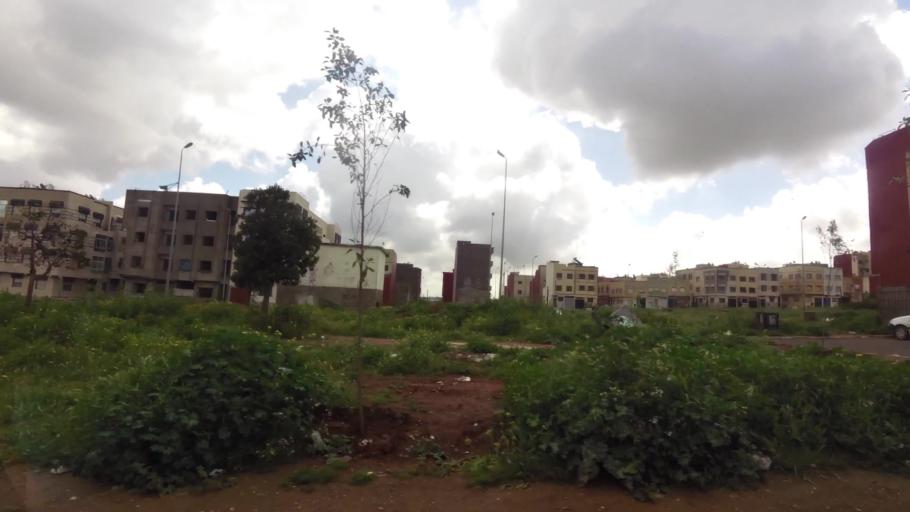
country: MA
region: Grand Casablanca
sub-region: Nouaceur
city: Bouskoura
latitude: 33.5072
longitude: -7.6508
